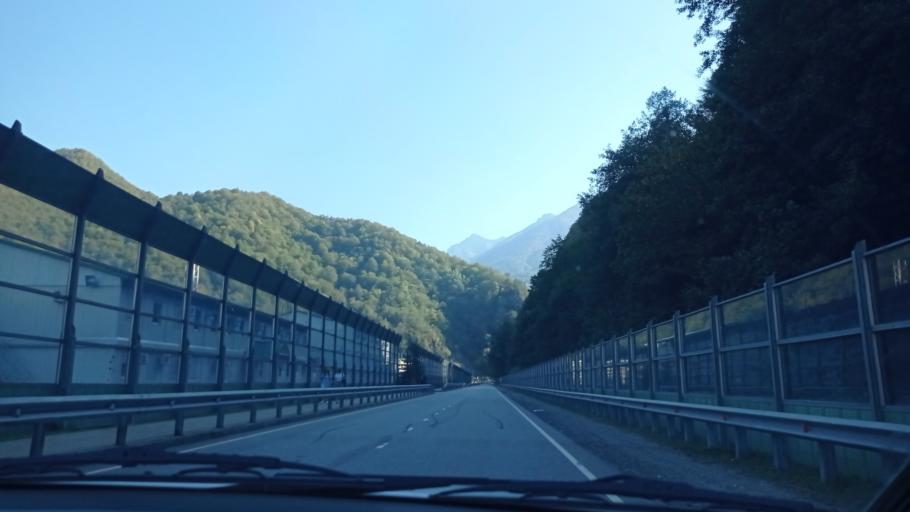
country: RU
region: Krasnodarskiy
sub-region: Sochi City
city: Krasnaya Polyana
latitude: 43.6875
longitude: 40.2753
